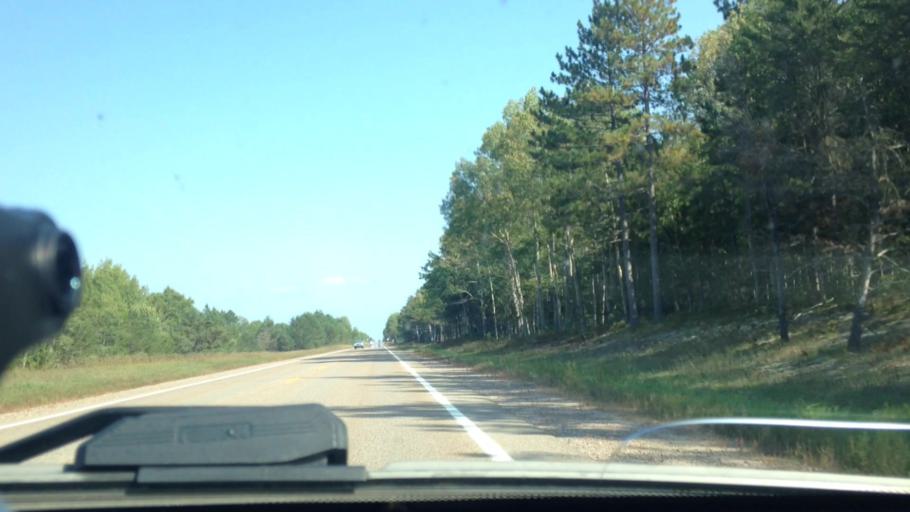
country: US
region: Michigan
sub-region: Mackinac County
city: Saint Ignace
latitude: 46.3583
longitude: -84.8740
